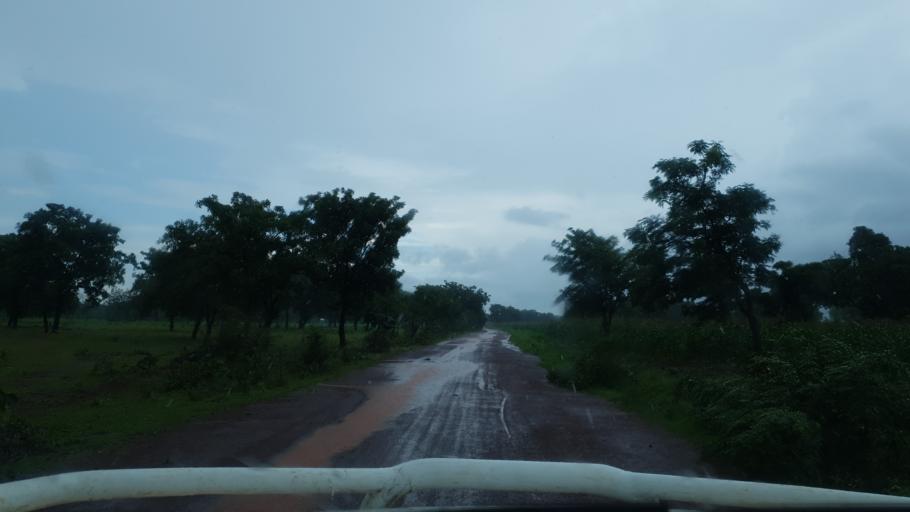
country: ML
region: Sikasso
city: Kolondieba
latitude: 11.5991
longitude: -6.6683
